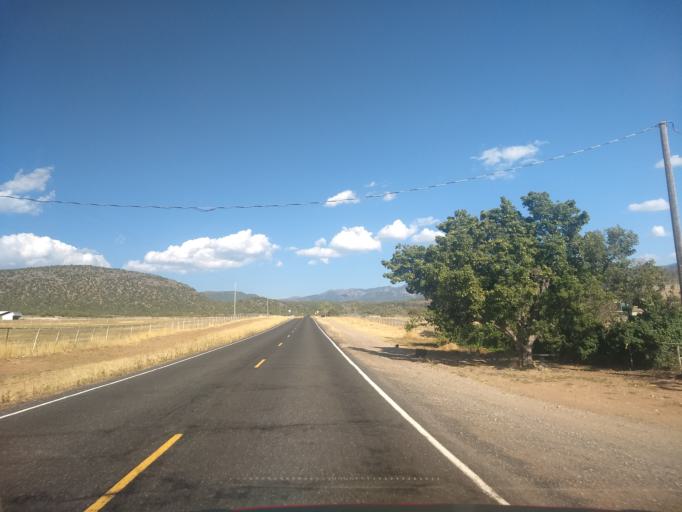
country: US
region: Utah
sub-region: Washington County
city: Enterprise
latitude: 37.4170
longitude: -113.6176
